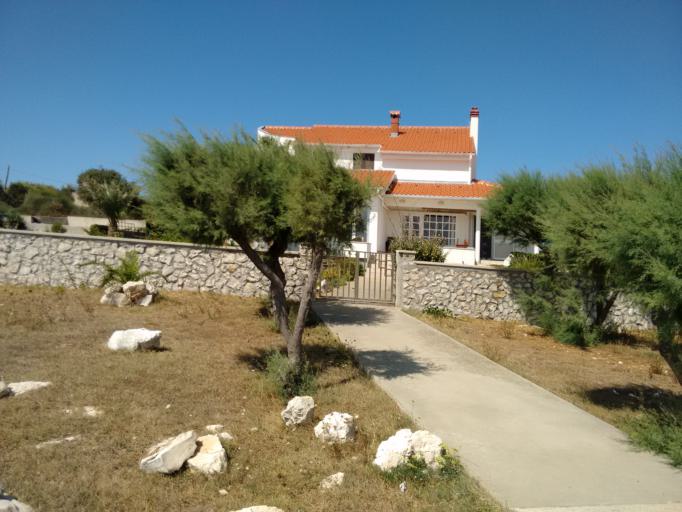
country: HR
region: Licko-Senjska
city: Novalja
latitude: 44.3730
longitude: 14.7026
